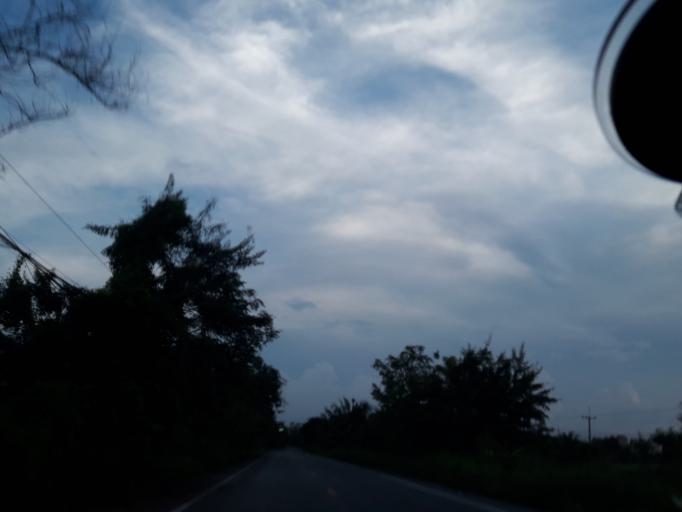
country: TH
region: Pathum Thani
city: Nong Suea
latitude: 14.1640
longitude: 100.8690
